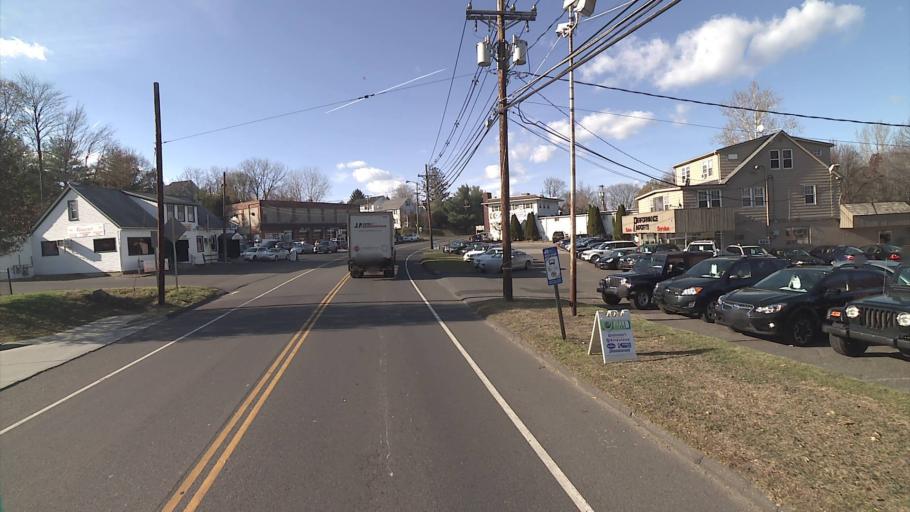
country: US
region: Connecticut
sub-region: Fairfield County
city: Bethel
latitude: 41.3850
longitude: -73.4273
